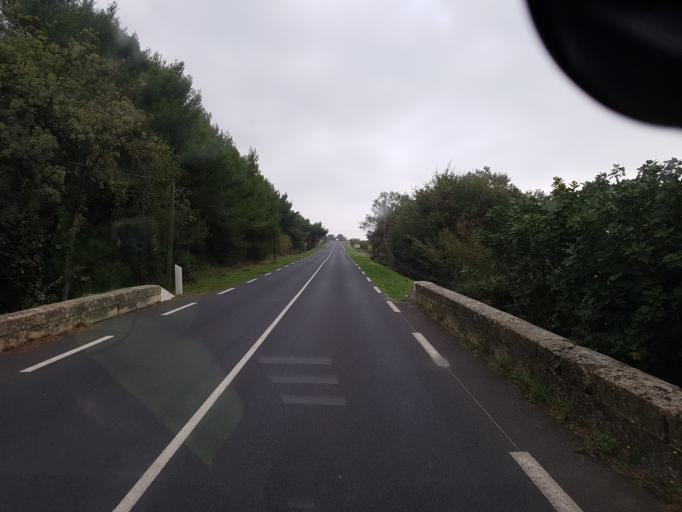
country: FR
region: Languedoc-Roussillon
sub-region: Departement de l'Herault
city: Pinet
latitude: 43.4241
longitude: 3.5521
